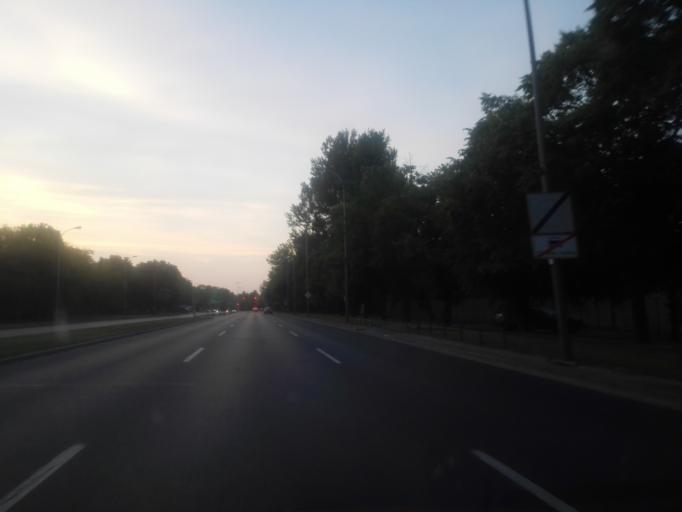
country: PL
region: Masovian Voivodeship
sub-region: Warszawa
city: Wlochy
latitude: 52.1771
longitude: 20.9790
